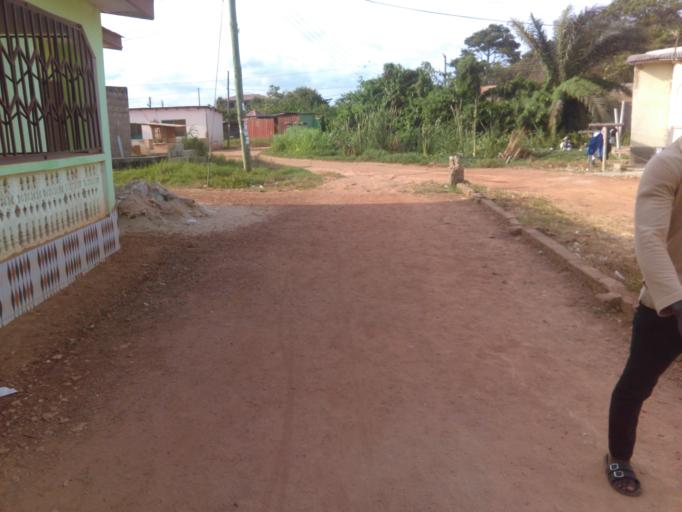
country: GH
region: Central
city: Cape Coast
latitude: 5.1143
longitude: -1.2967
